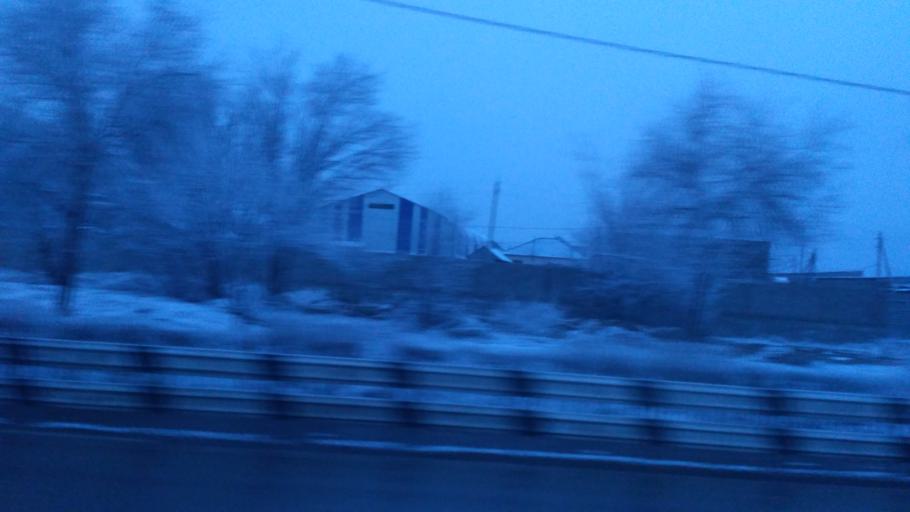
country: KZ
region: Ongtustik Qazaqstan
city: Shymkent
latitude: 42.3559
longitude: 69.5249
